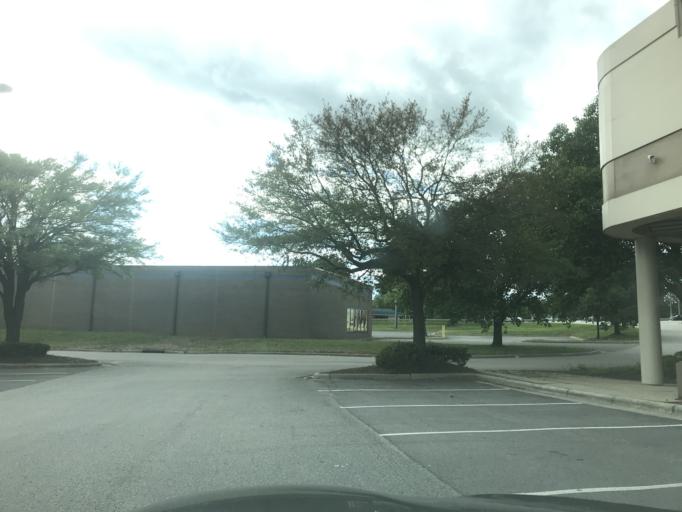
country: US
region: North Carolina
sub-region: Wake County
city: Raleigh
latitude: 35.8365
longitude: -78.5799
